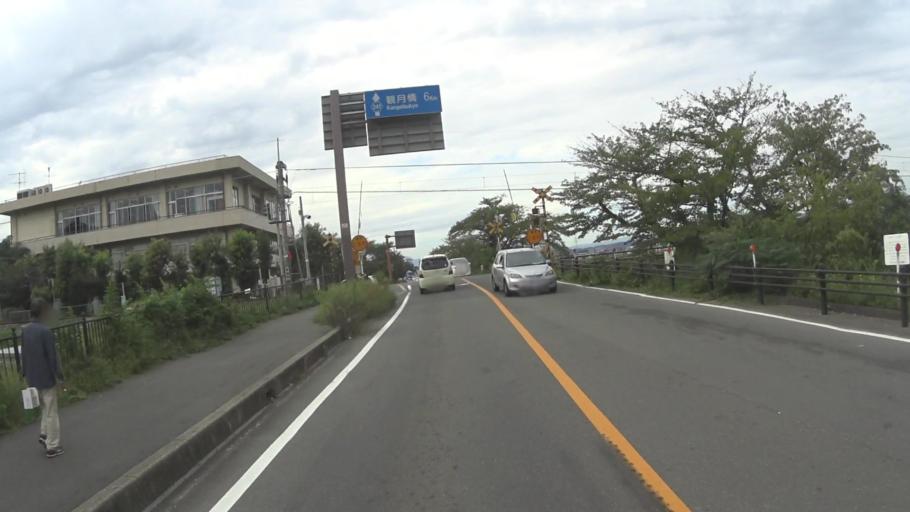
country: JP
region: Kyoto
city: Uji
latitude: 34.8926
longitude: 135.8053
